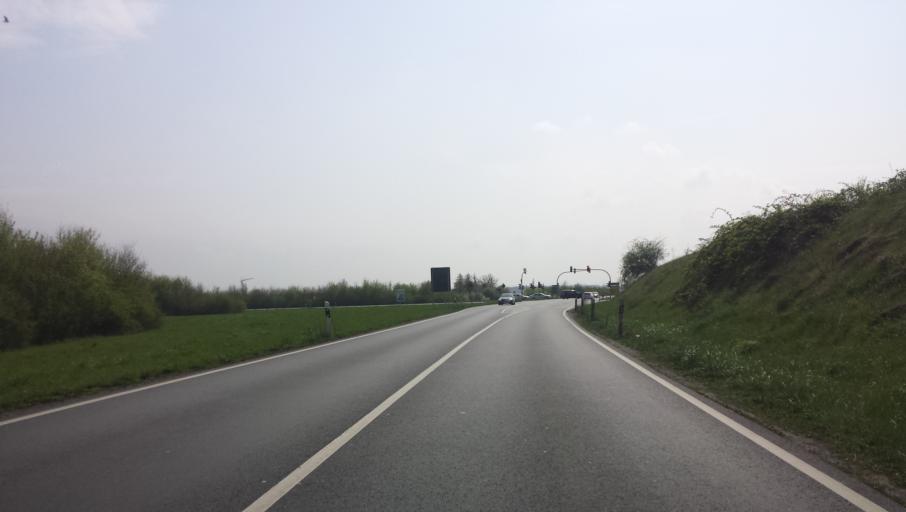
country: DE
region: Hesse
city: Gernsheim
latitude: 49.7554
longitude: 8.5056
